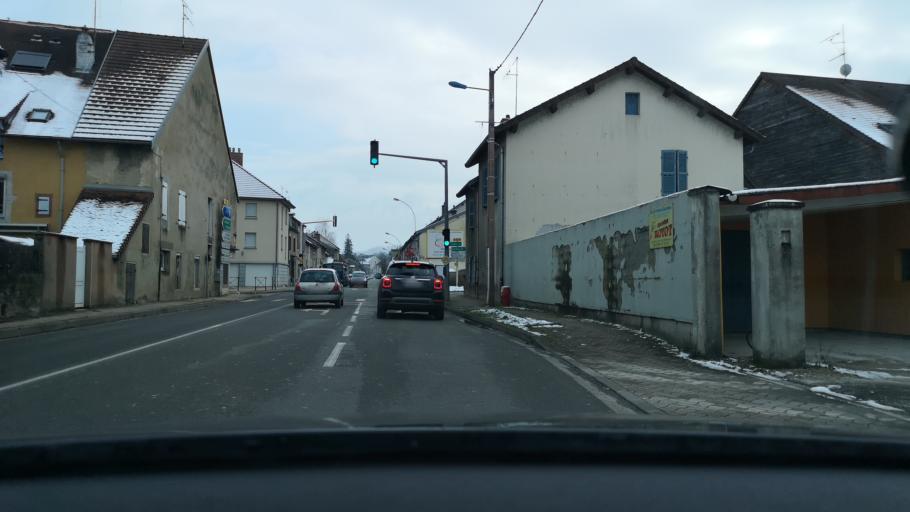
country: FR
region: Franche-Comte
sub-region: Departement du Jura
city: Montmorot
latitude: 46.6757
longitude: 5.5298
